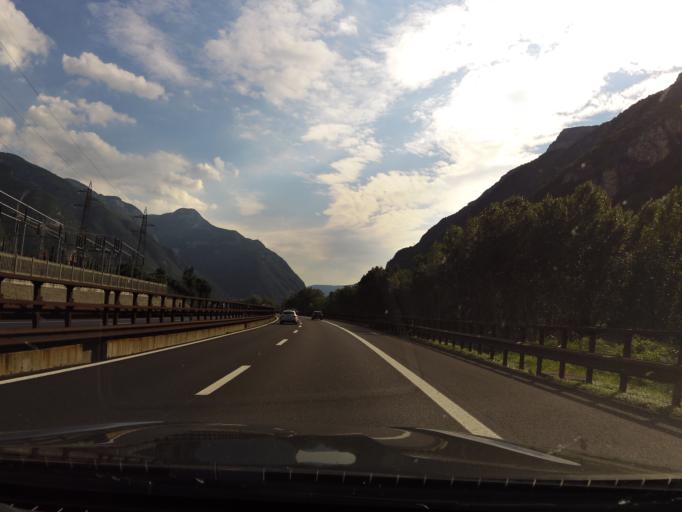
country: IT
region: Trentino-Alto Adige
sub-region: Provincia di Trento
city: Ala
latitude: 45.7640
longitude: 10.9990
